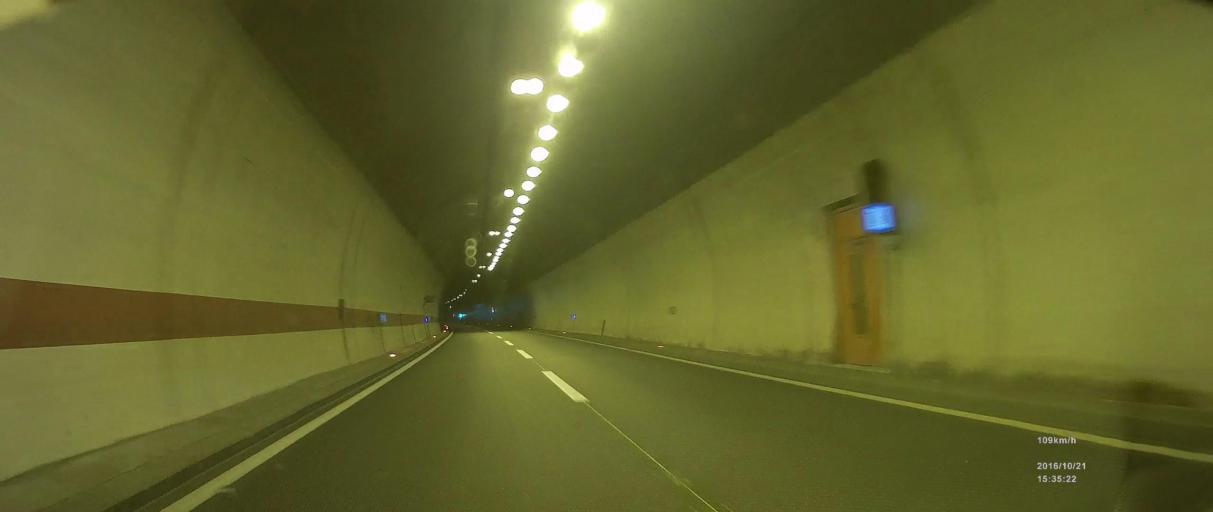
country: HR
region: Zadarska
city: Obrovac
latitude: 44.2566
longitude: 15.6507
